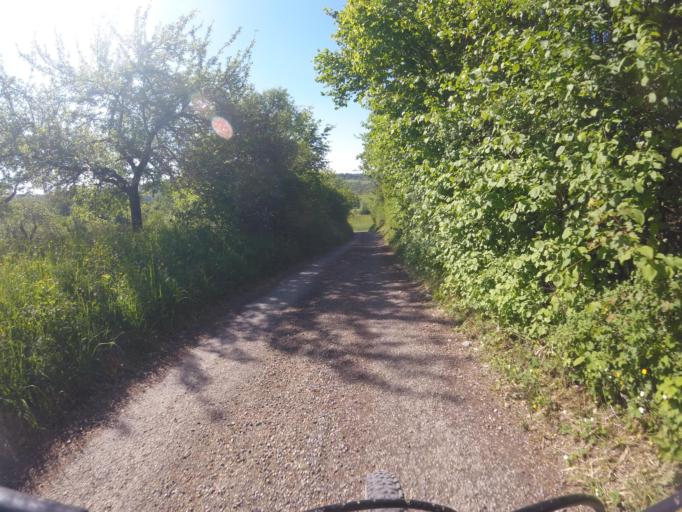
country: DE
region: Baden-Wuerttemberg
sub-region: Regierungsbezirk Stuttgart
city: Aspach
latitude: 48.9963
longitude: 9.4122
